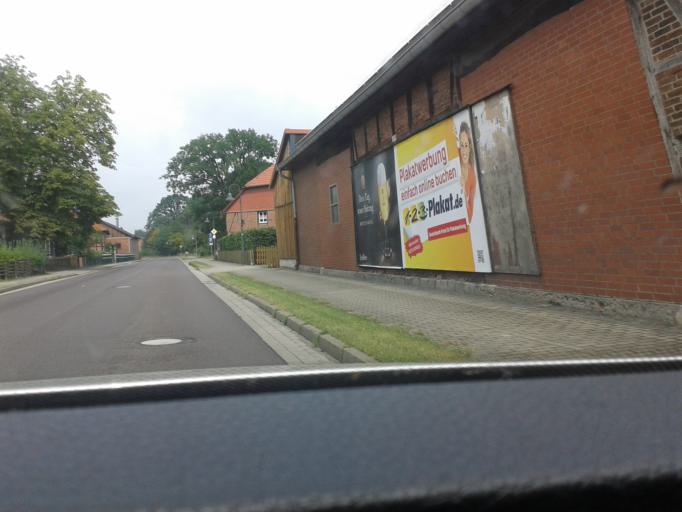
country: DE
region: Lower Saxony
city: Sassenburg
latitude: 52.4883
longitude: 10.6311
